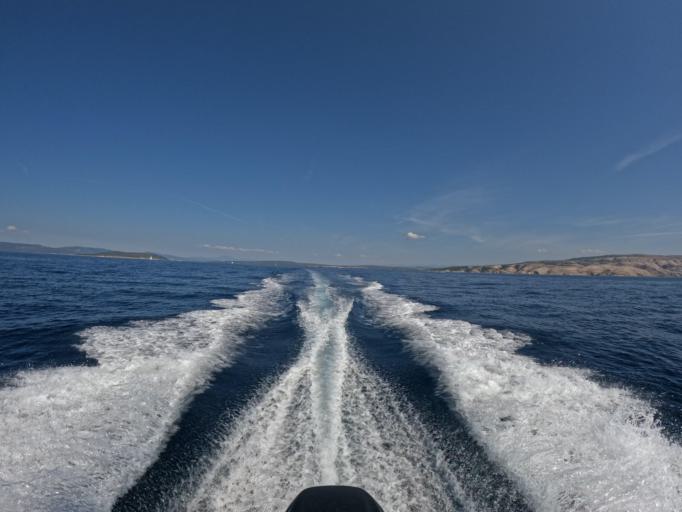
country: HR
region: Primorsko-Goranska
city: Punat
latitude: 44.9288
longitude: 14.6186
